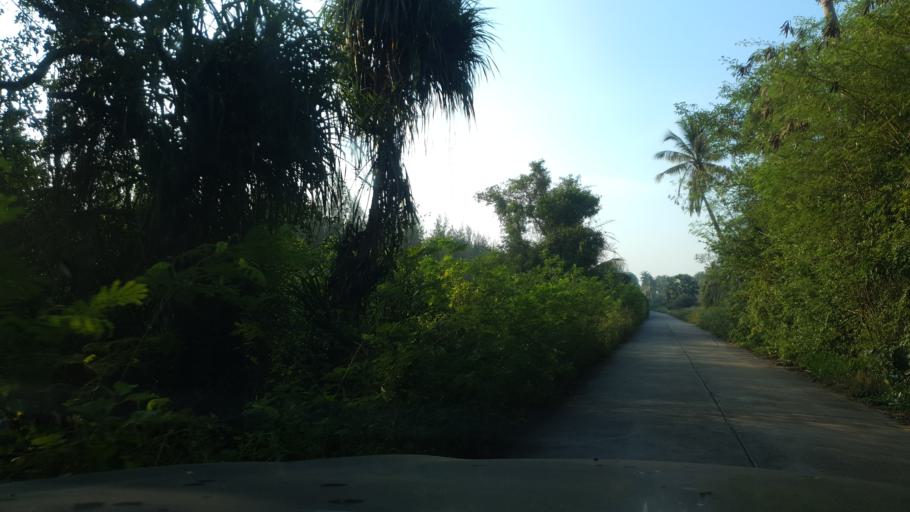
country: TH
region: Prachuap Khiri Khan
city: Bang Saphan
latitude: 11.3036
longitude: 99.5503
